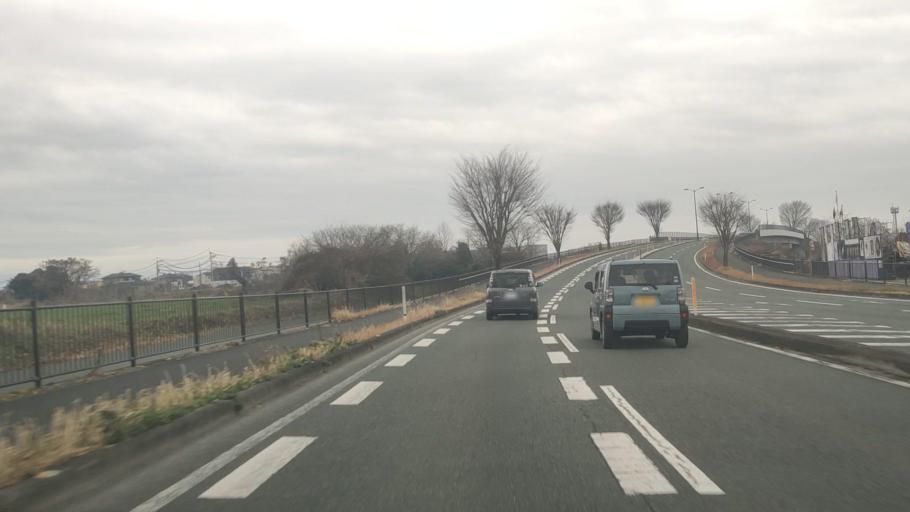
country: JP
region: Kumamoto
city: Ozu
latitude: 32.8208
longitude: 130.7909
